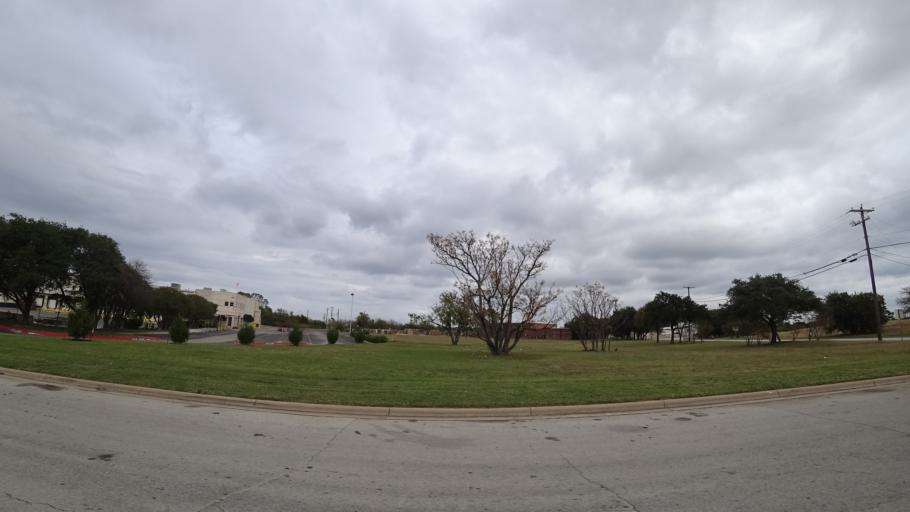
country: US
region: Texas
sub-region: Williamson County
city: Round Rock
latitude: 30.5037
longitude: -97.6890
